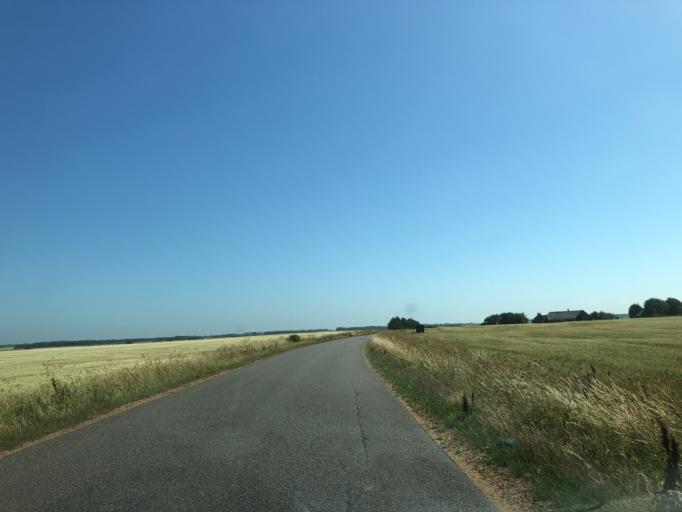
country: DK
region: Central Jutland
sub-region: Holstebro Kommune
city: Ulfborg
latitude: 56.2996
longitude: 8.2083
